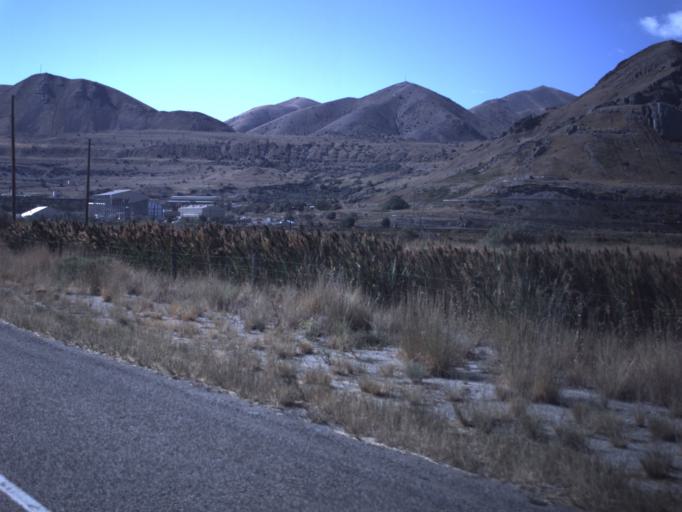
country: US
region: Utah
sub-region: Salt Lake County
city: Magna
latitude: 40.7362
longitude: -112.1725
